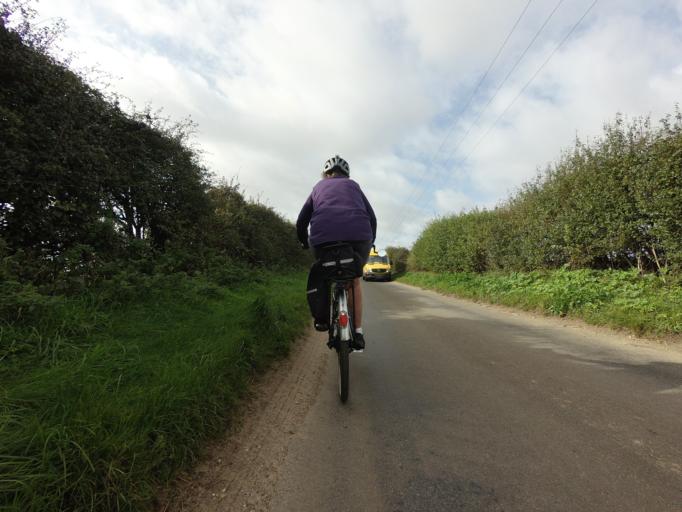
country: GB
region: England
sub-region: Norfolk
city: Hunstanton
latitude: 52.9367
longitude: 0.6626
